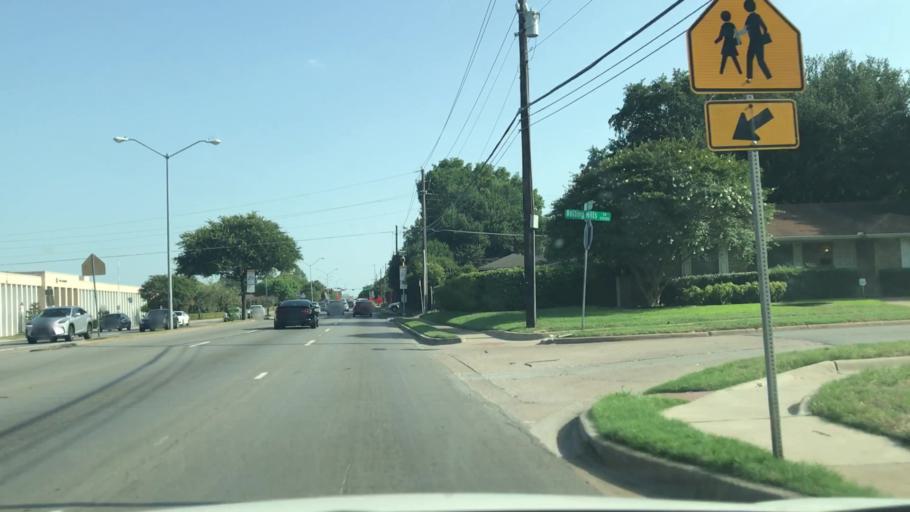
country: US
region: Texas
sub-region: Dallas County
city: Richardson
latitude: 32.9365
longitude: -96.7691
